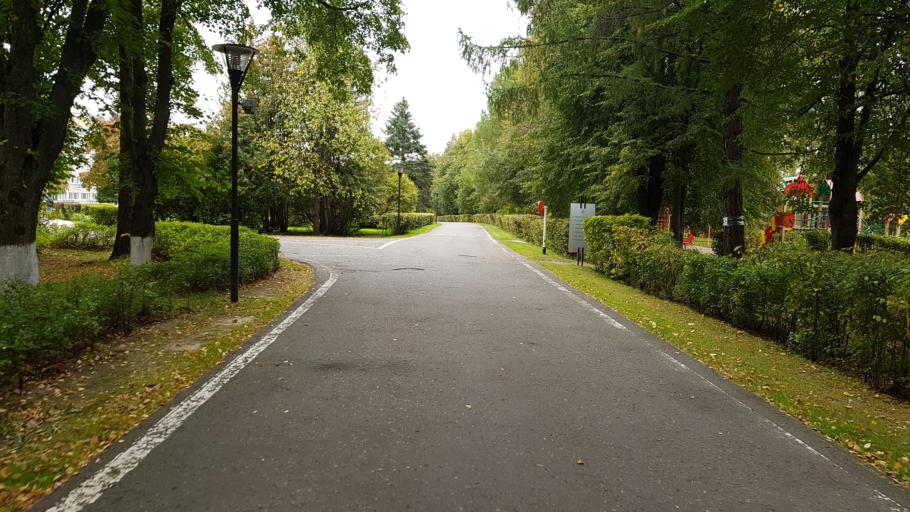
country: RU
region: Moskovskaya
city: Filimonki
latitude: 55.5229
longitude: 37.4050
